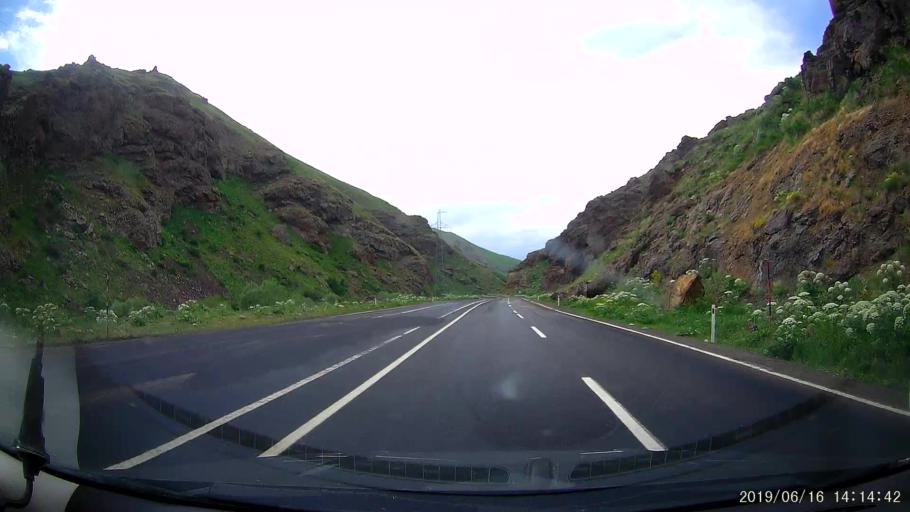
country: TR
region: Agri
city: Tahir
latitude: 39.7972
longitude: 42.4918
